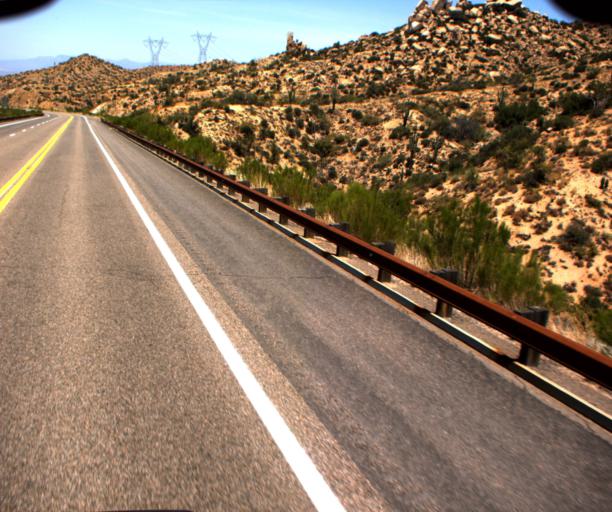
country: US
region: Arizona
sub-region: Gila County
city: Miami
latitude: 33.5421
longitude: -110.9382
